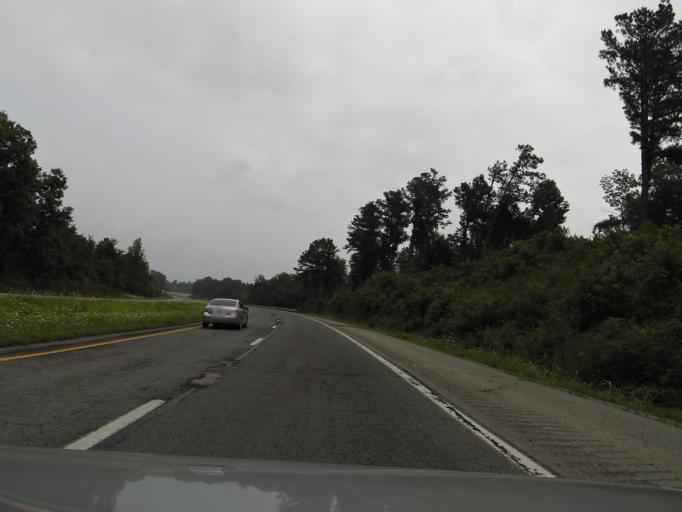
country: US
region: Kentucky
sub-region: Muhlenberg County
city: Central City
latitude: 37.2886
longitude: -87.0849
